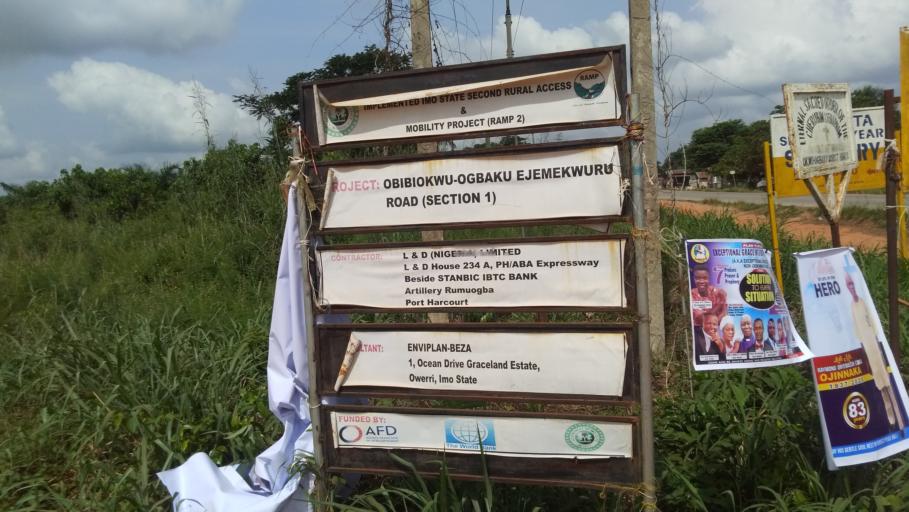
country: NG
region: Imo
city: Orodo
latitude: 5.5753
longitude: 6.9479
